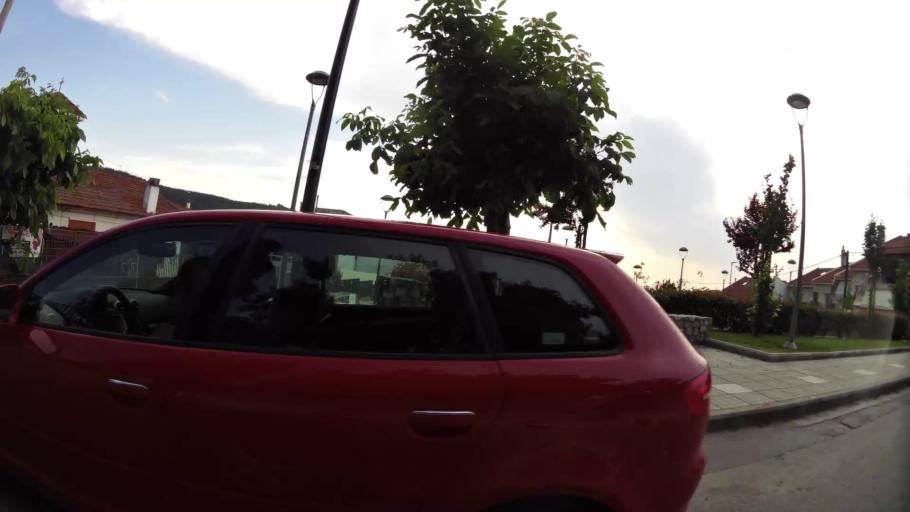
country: GR
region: Central Macedonia
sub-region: Nomos Thessalonikis
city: Pefka
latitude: 40.6588
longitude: 22.9888
